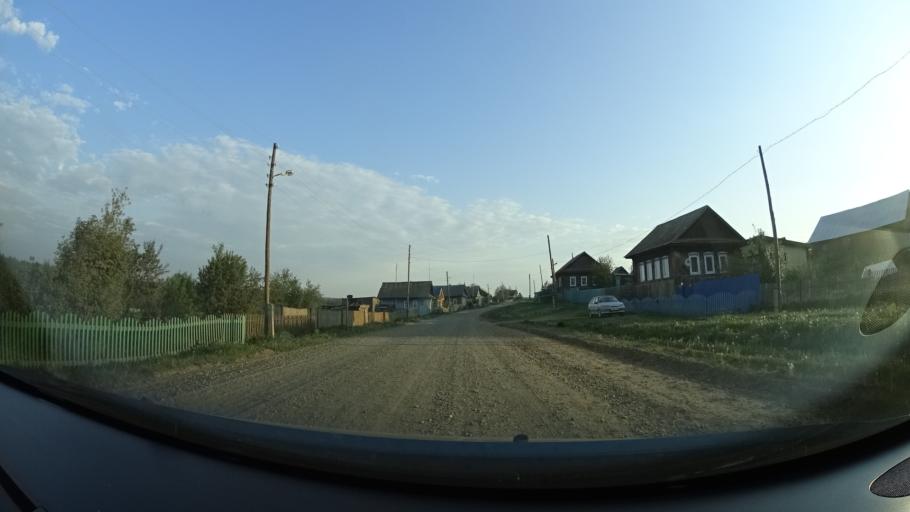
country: RU
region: Perm
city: Barda
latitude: 56.6824
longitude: 55.6901
